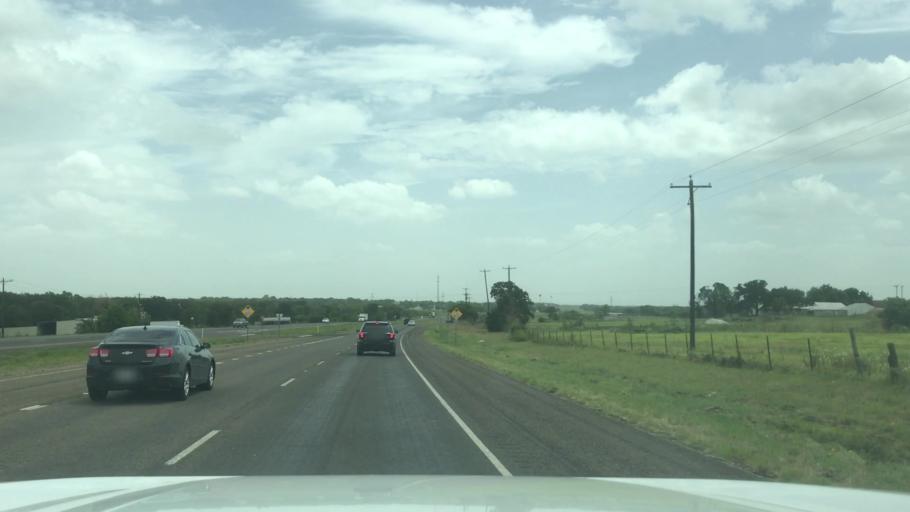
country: US
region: Texas
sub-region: McLennan County
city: Riesel
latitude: 31.4894
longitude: -96.9285
